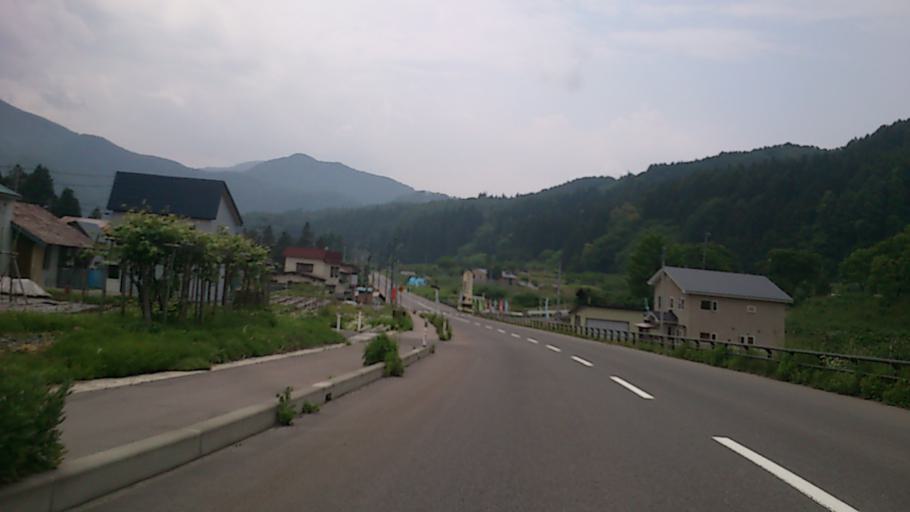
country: JP
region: Aomori
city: Hirosaki
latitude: 40.5494
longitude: 140.2743
